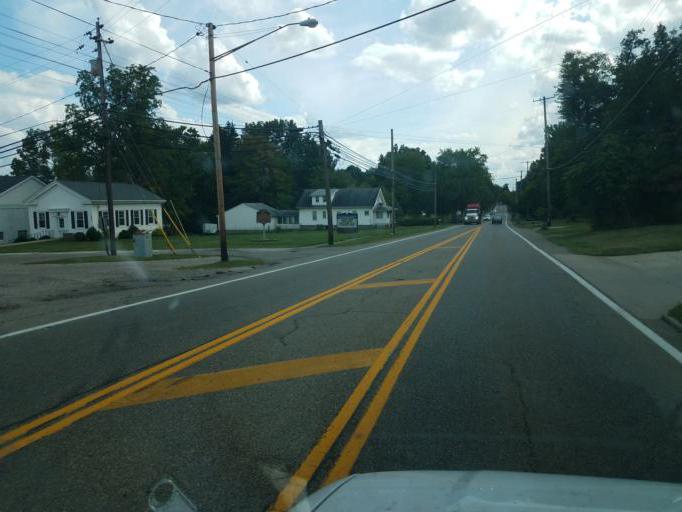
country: US
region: Ohio
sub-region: Portage County
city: Ravenna
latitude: 41.0984
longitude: -81.2426
